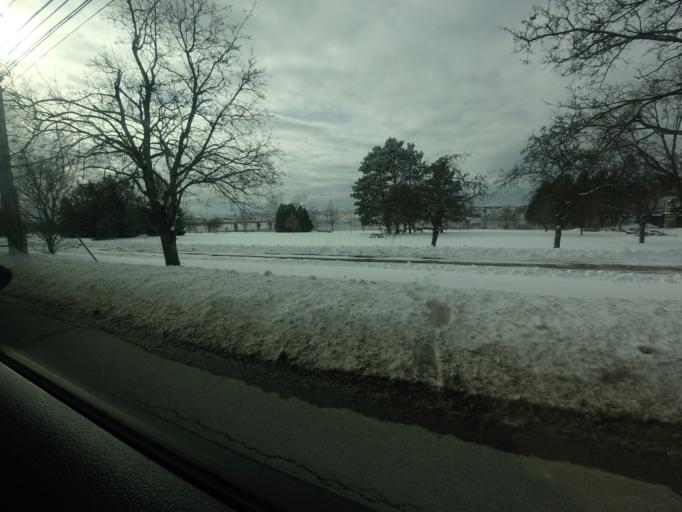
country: CA
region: New Brunswick
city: Fredericton
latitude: 45.9631
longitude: -66.6259
